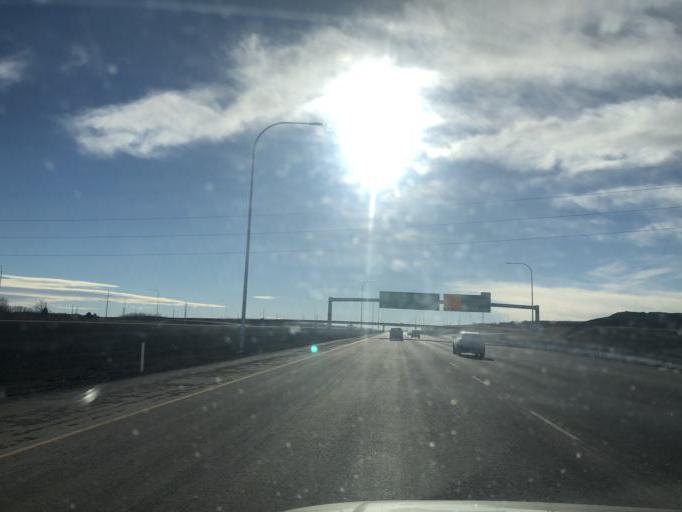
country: CA
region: Alberta
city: Calgary
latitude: 50.9813
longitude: -114.1624
